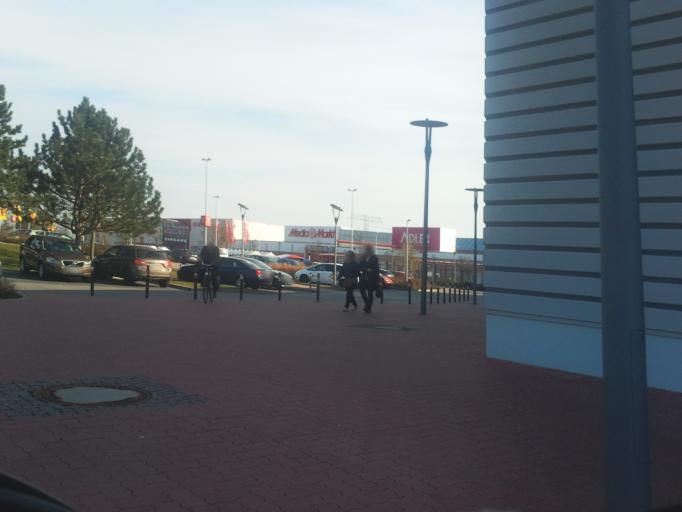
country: DE
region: Mecklenburg-Vorpommern
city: Lambrechtshagen
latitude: 54.1068
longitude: 12.0334
